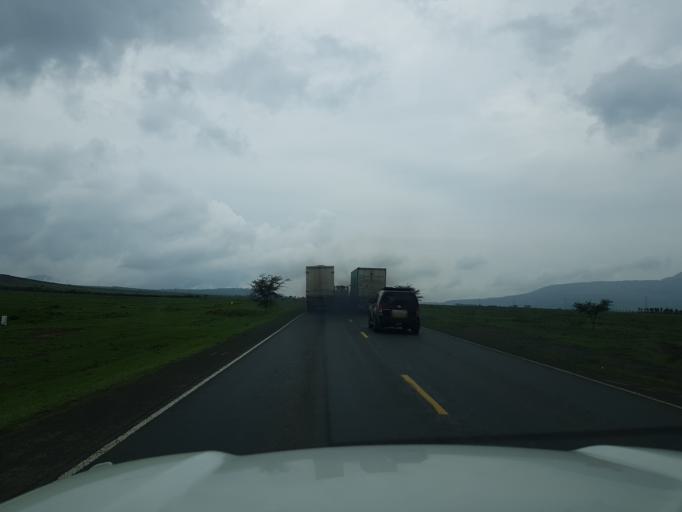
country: KE
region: Nakuru
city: Naivasha
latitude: -0.8337
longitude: 36.4729
